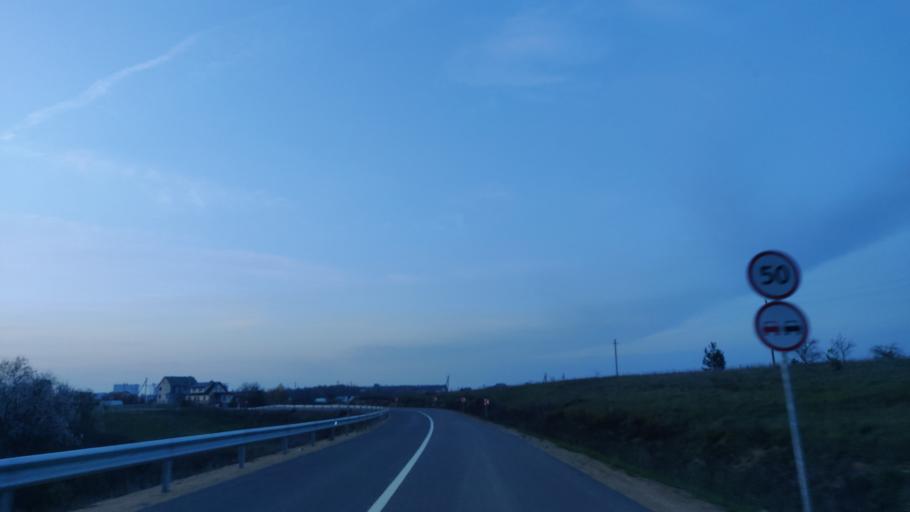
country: LT
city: Trakai
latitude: 54.6084
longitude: 24.9933
